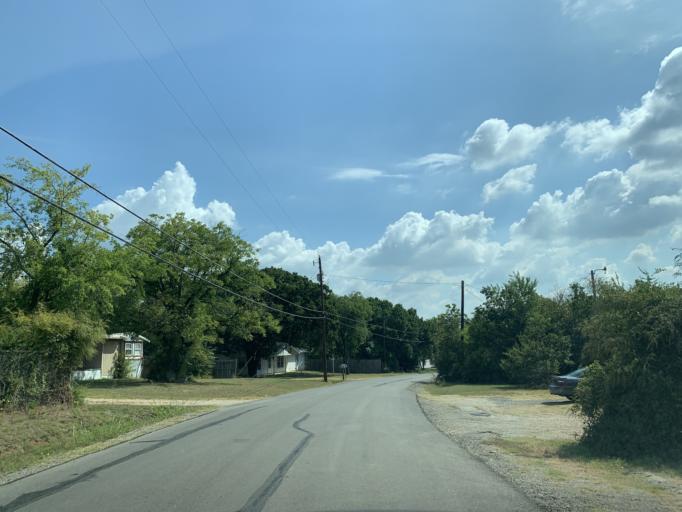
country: US
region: Texas
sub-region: Tarrant County
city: Azle
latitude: 32.8690
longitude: -97.5291
